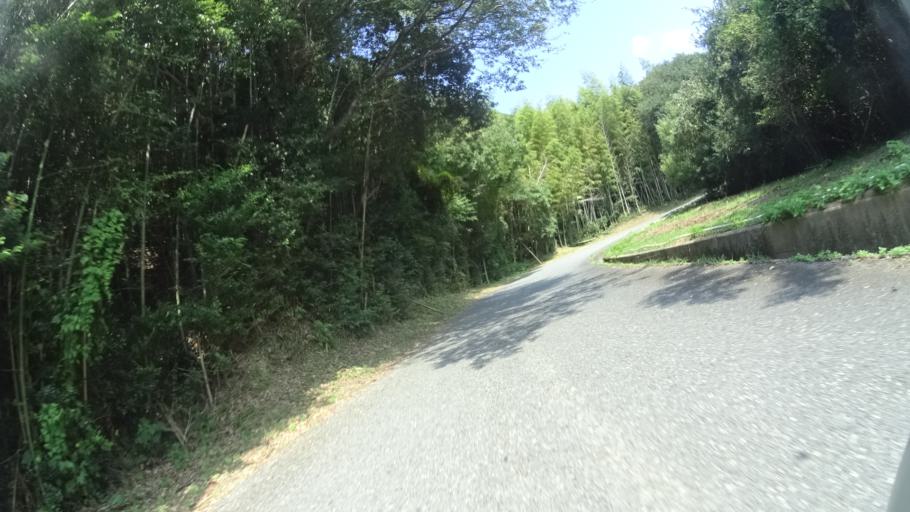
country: JP
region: Yamaguchi
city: Shimonoseki
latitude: 34.1068
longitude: 130.8680
